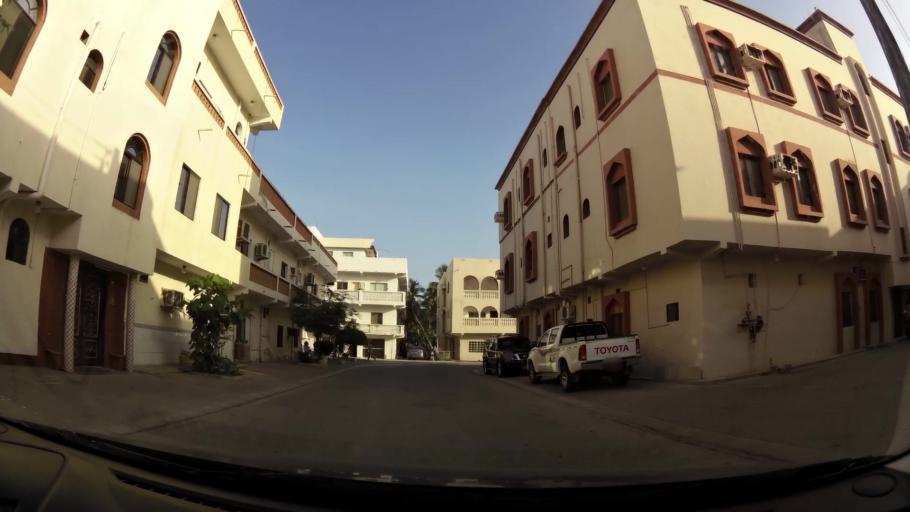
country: OM
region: Zufar
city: Salalah
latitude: 17.0083
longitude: 54.0807
